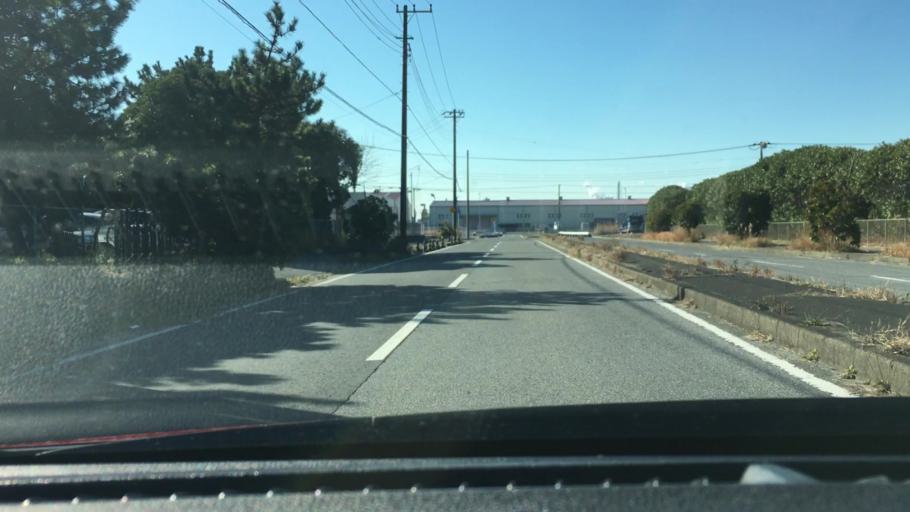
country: JP
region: Chiba
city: Kisarazu
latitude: 35.3745
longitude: 139.9092
